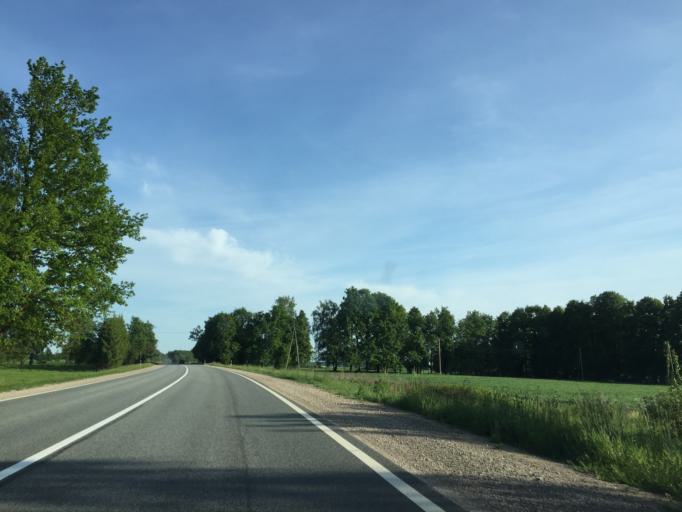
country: LV
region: Lecava
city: Iecava
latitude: 56.5278
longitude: 24.1705
